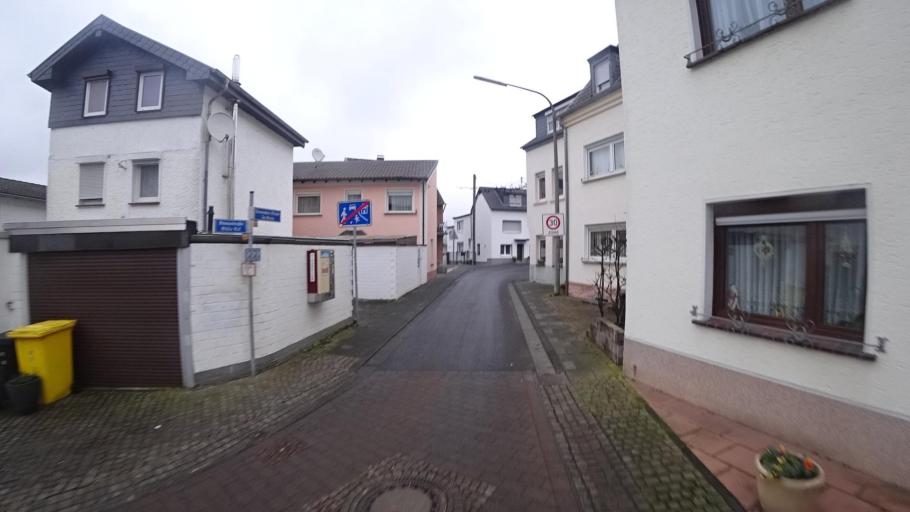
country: DE
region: Rheinland-Pfalz
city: Bad Neuenahr-Ahrweiler
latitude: 50.5401
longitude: 7.1128
